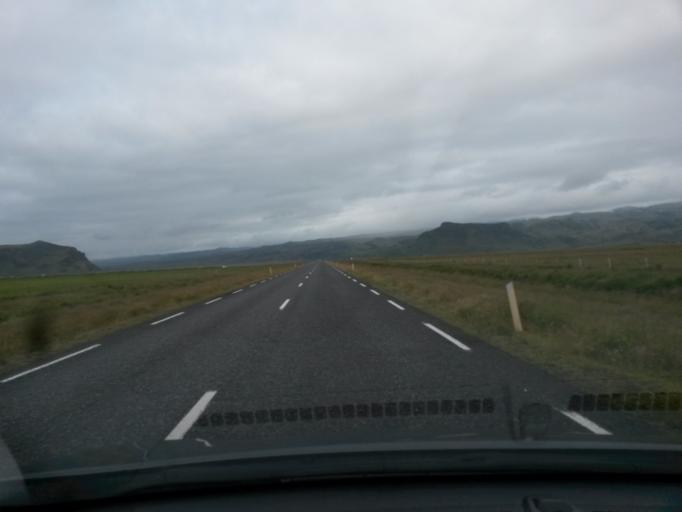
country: IS
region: South
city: Vestmannaeyjar
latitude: 63.4445
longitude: -19.2009
